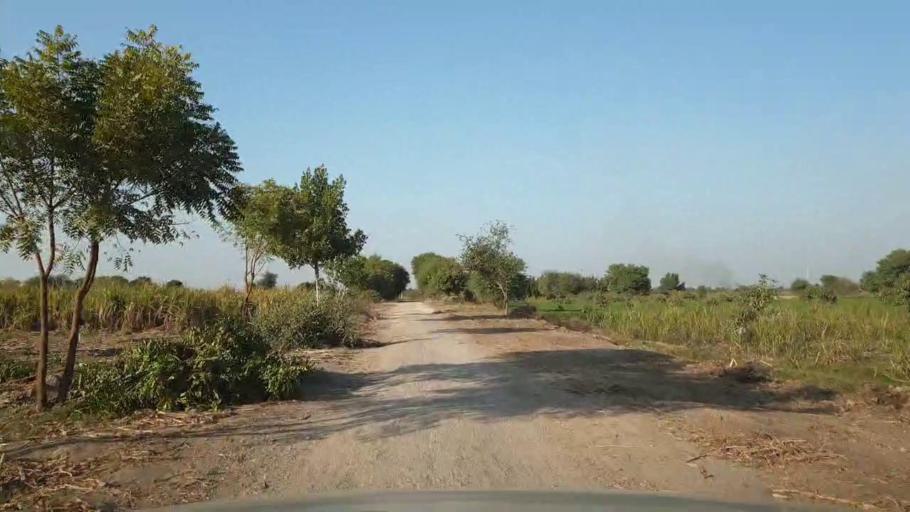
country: PK
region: Sindh
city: Tando Allahyar
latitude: 25.5000
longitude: 68.6490
